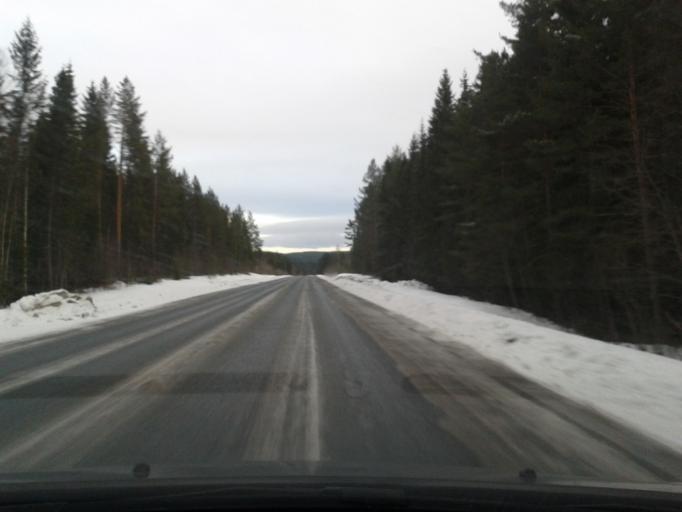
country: SE
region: Vaesternorrland
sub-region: Solleftea Kommun
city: As
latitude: 63.4407
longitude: 16.9223
